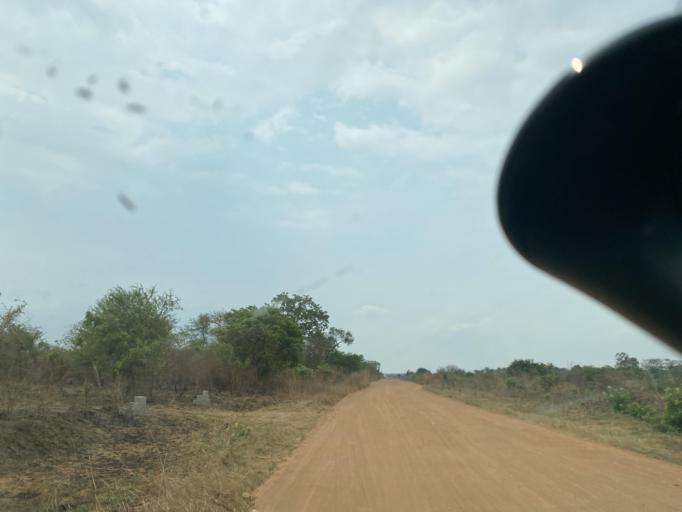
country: ZM
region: Lusaka
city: Lusaka
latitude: -15.2032
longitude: 28.3409
